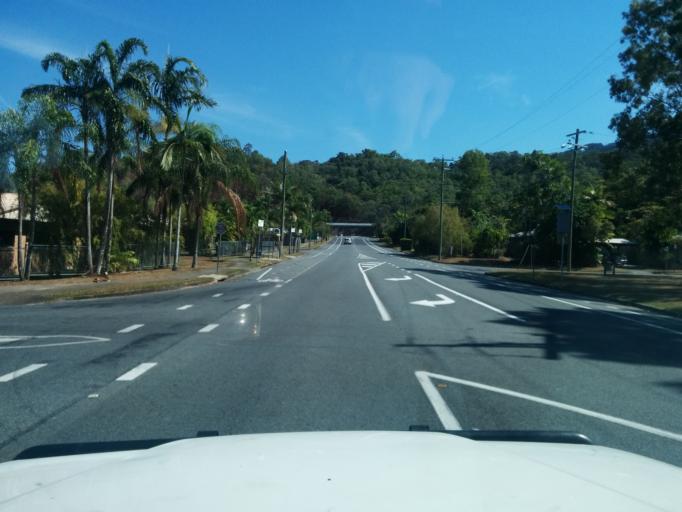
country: AU
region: Queensland
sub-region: Cairns
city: Cairns
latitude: -16.9119
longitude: 145.7280
